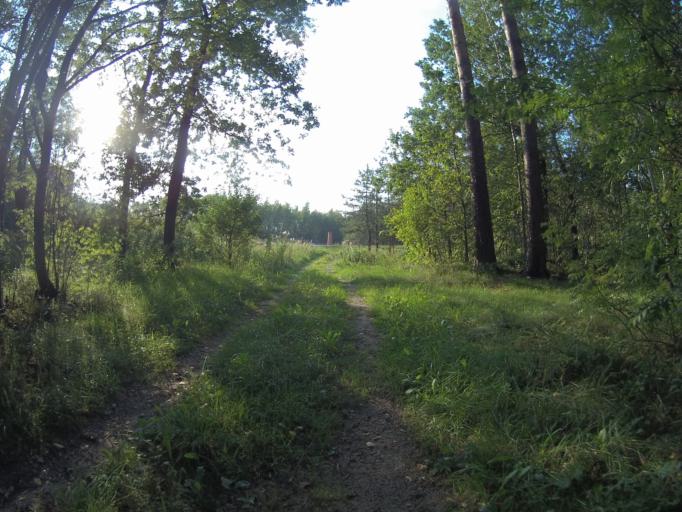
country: RU
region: Vladimir
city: Kommunar
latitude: 56.0641
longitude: 40.4589
